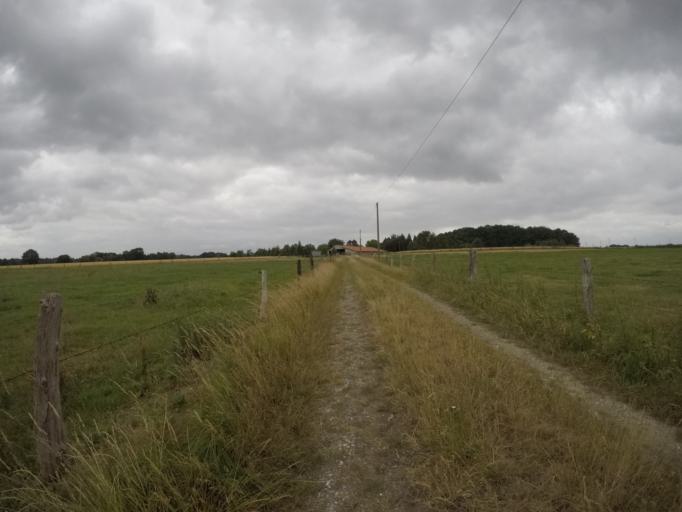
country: DE
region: North Rhine-Westphalia
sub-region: Regierungsbezirk Dusseldorf
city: Bocholt
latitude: 51.7931
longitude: 6.6239
